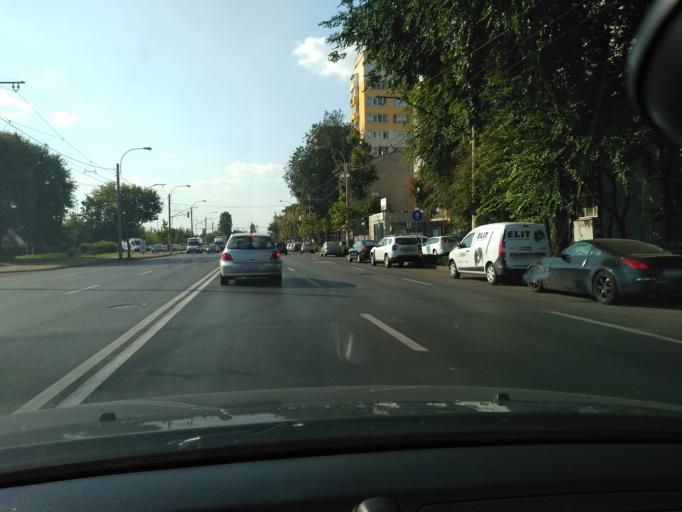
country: RO
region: Bucuresti
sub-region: Municipiul Bucuresti
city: Bucuresti
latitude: 44.4528
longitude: 26.0657
